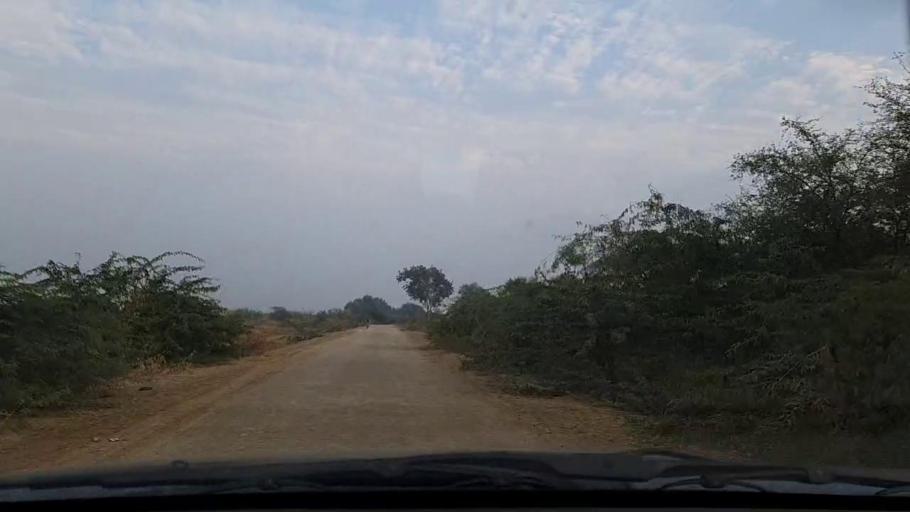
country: PK
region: Sindh
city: Pithoro
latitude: 25.6002
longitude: 69.4587
